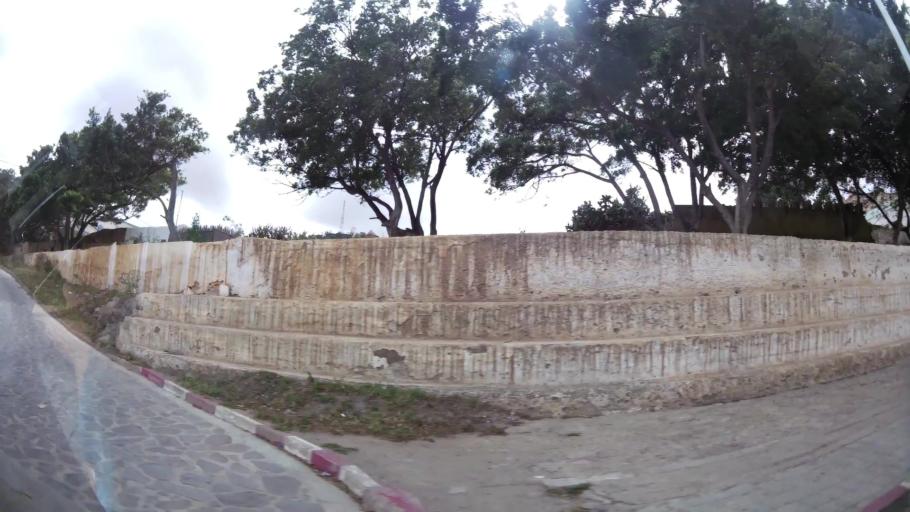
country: MA
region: Oriental
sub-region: Nador
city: Nador
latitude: 35.1870
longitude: -2.9287
